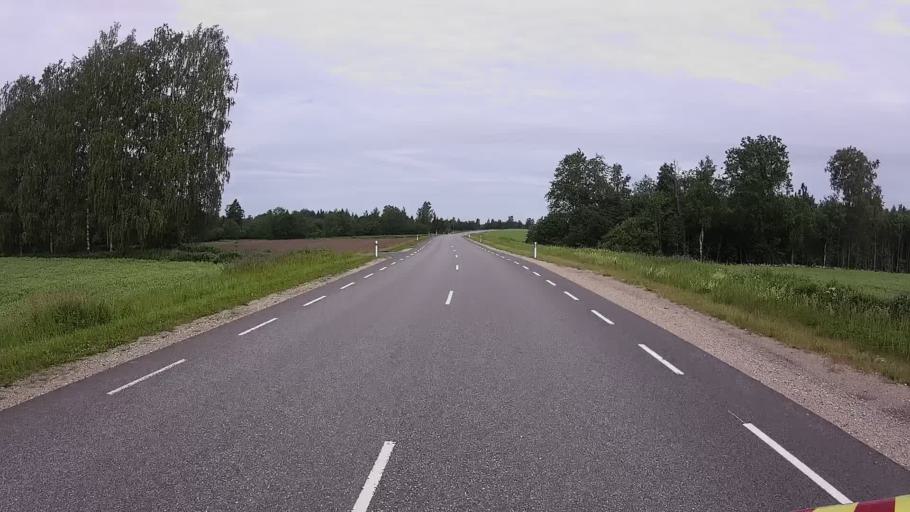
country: EE
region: Viljandimaa
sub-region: Karksi vald
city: Karksi-Nuia
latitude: 58.1588
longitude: 25.5925
